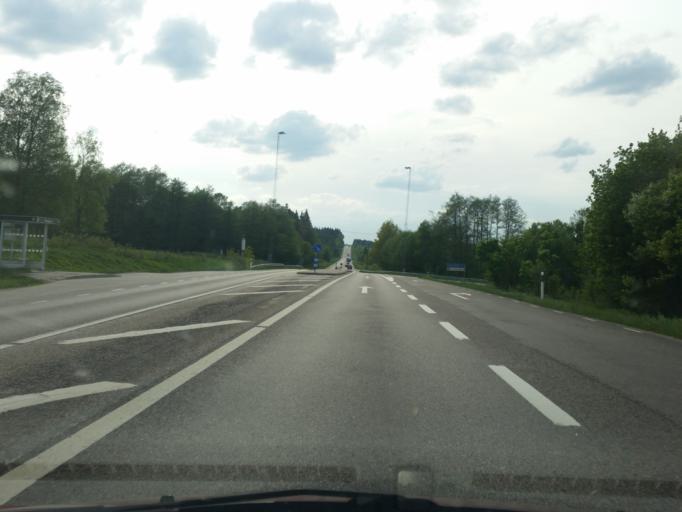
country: SE
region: Vaestra Goetaland
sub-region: Ulricehamns Kommun
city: Ulricehamn
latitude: 57.8076
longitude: 13.2413
